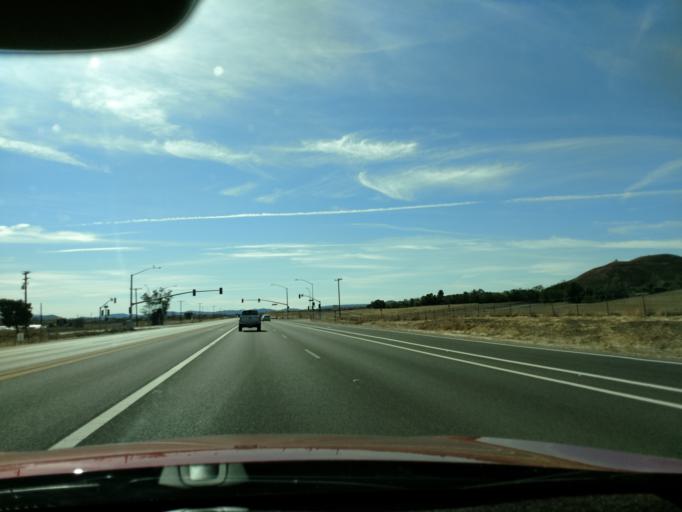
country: US
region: California
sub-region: Riverside County
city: Winchester
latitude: 33.6283
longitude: -117.0926
